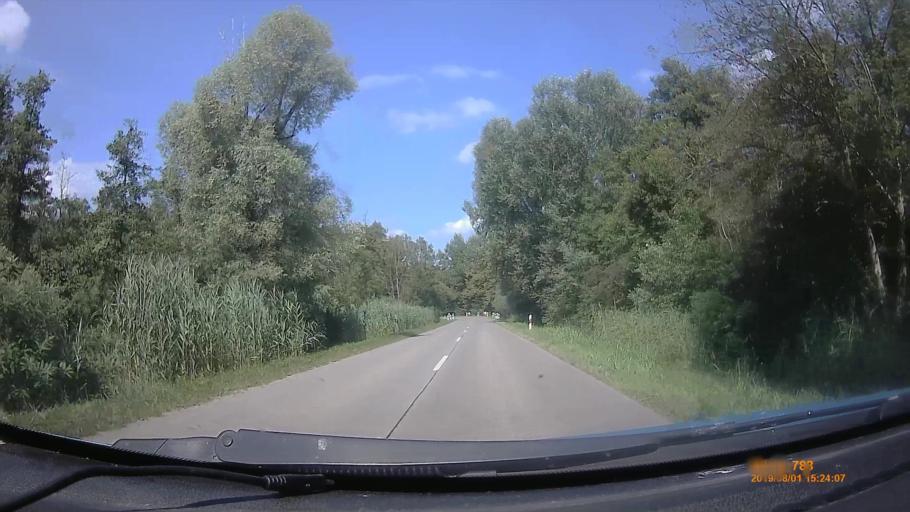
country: HU
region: Baranya
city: Sellye
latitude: 45.8822
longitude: 17.8493
